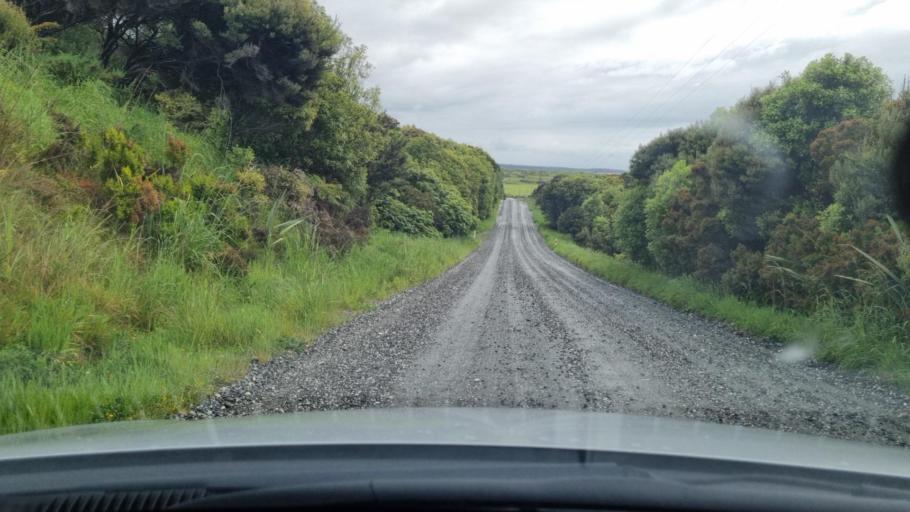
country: NZ
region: Southland
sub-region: Invercargill City
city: Bluff
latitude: -46.5248
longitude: 168.2706
